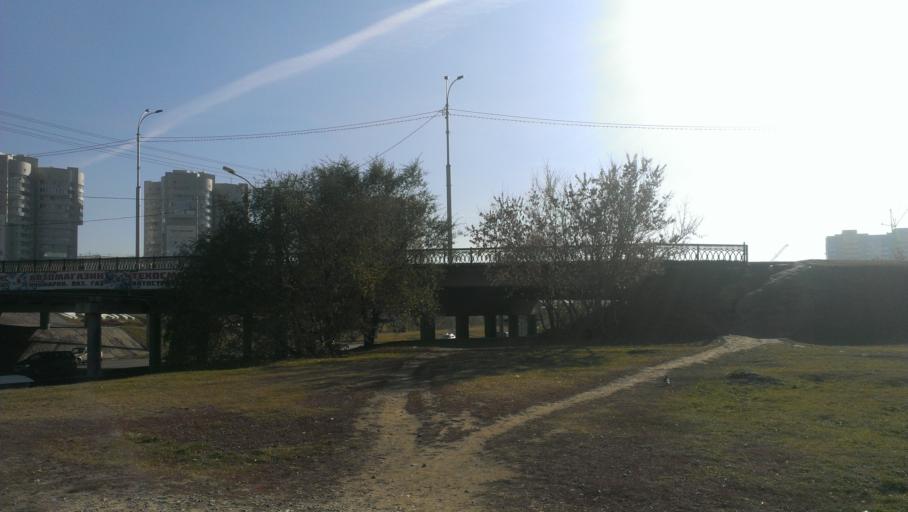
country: RU
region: Altai Krai
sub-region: Gorod Barnaulskiy
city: Barnaul
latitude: 53.3432
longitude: 83.6950
